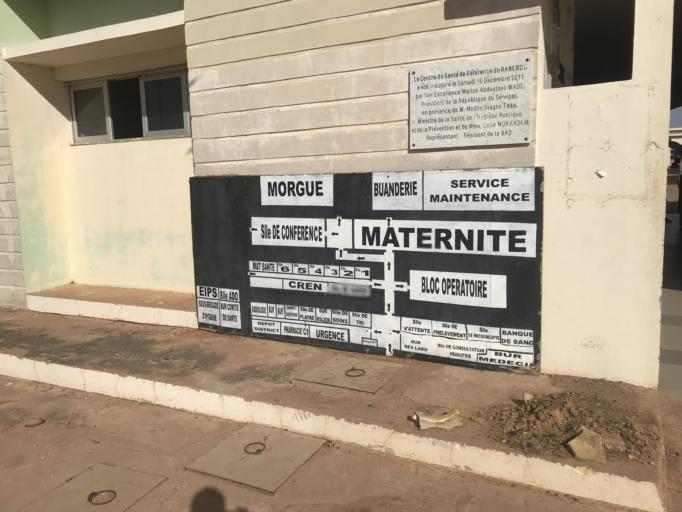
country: SN
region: Matam
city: Ranerou
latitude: 15.3038
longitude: -13.9591
